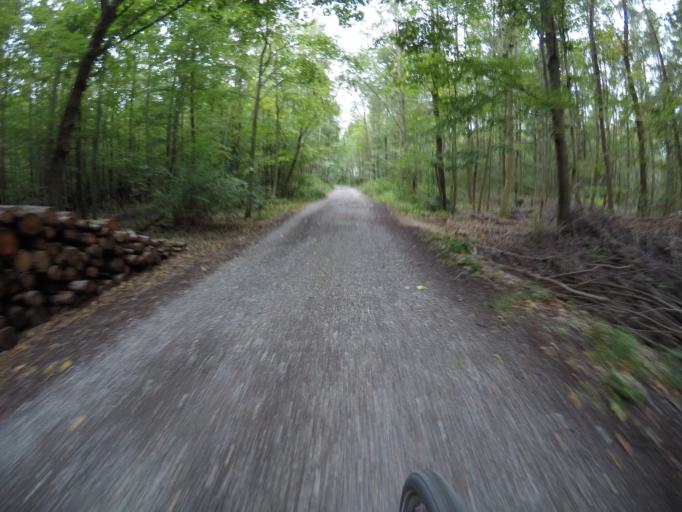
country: DE
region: Baden-Wuerttemberg
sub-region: Regierungsbezirk Stuttgart
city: Eberdingen
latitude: 48.8718
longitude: 8.9909
